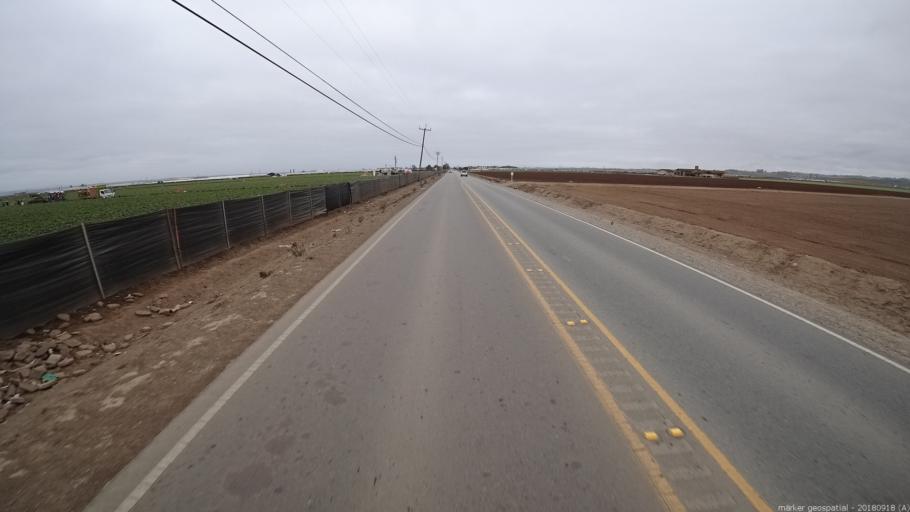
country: US
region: California
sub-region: Monterey County
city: Prunedale
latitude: 36.7372
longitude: -121.6659
